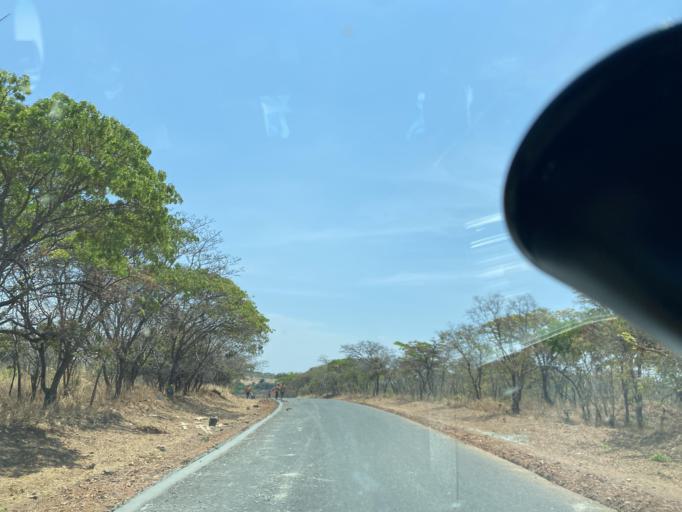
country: ZM
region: Lusaka
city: Kafue
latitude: -15.8440
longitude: 28.4120
